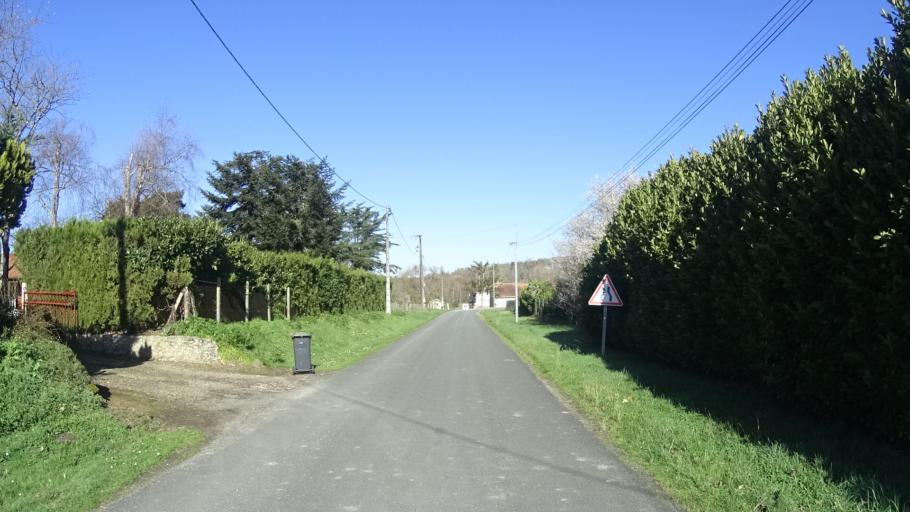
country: FR
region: Aquitaine
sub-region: Departement de la Dordogne
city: Saint-Aulaye
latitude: 45.2220
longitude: 0.1020
